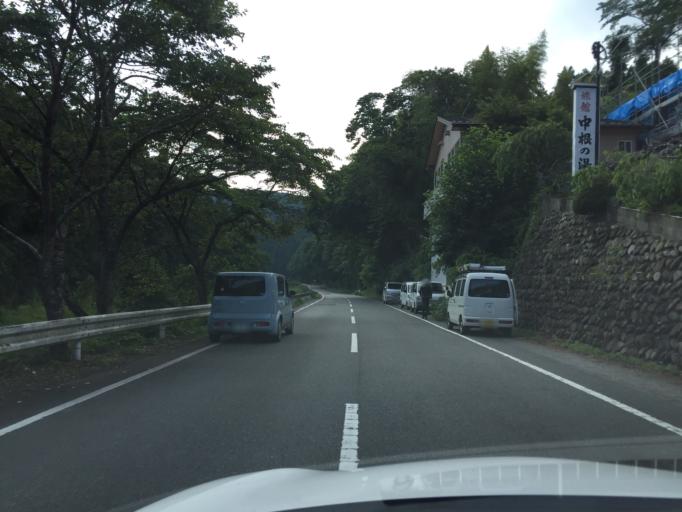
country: JP
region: Fukushima
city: Iwaki
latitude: 37.0098
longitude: 140.7165
